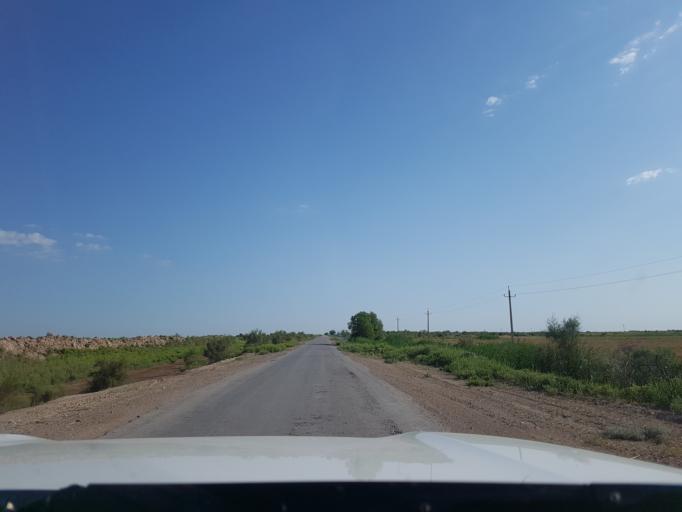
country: TM
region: Dasoguz
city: Koeneuergench
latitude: 41.9154
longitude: 58.7107
